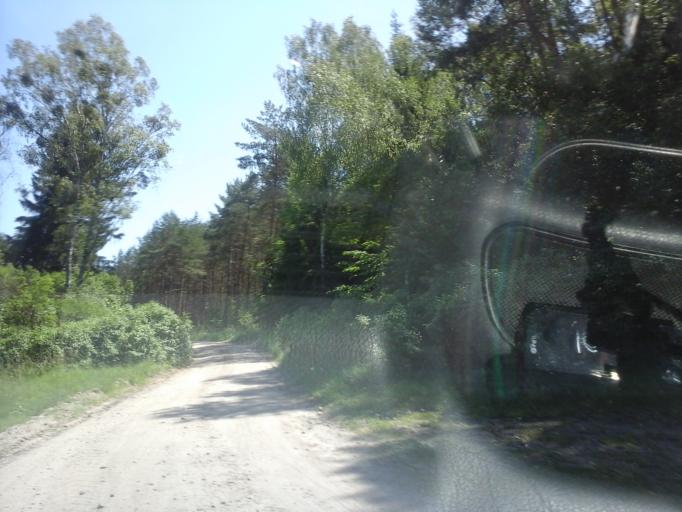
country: PL
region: West Pomeranian Voivodeship
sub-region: Powiat drawski
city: Kalisz Pomorski
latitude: 53.1614
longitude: 15.9111
